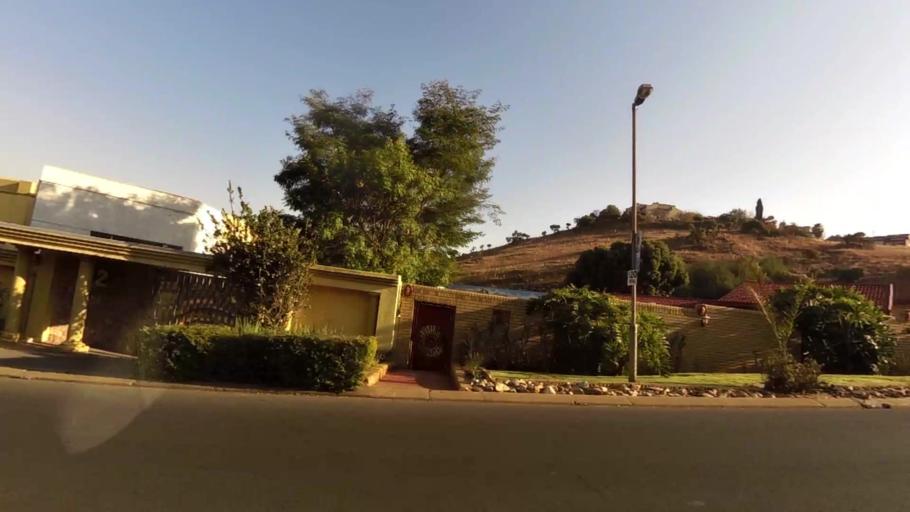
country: ZA
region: Gauteng
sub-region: City of Johannesburg Metropolitan Municipality
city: Soweto
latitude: -26.2815
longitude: 27.9575
